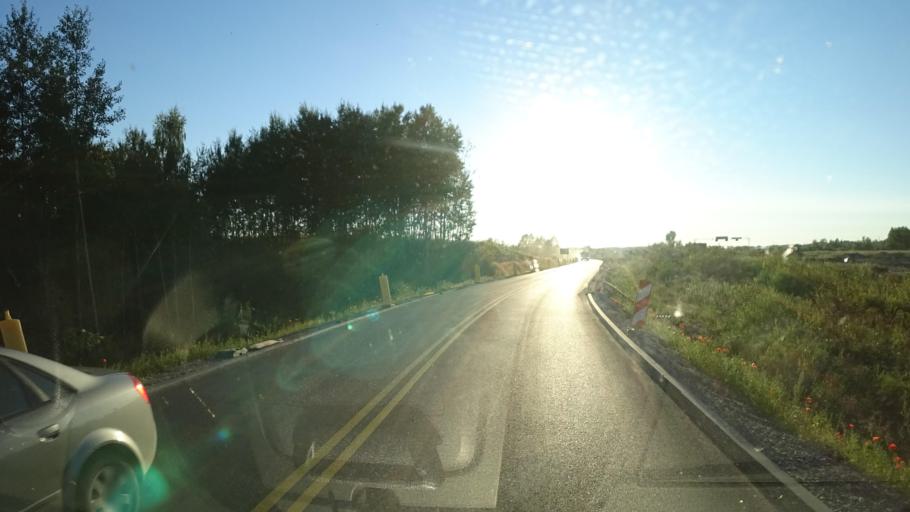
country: PL
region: Warmian-Masurian Voivodeship
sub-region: Powiat elcki
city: Elk
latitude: 53.8443
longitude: 22.3777
